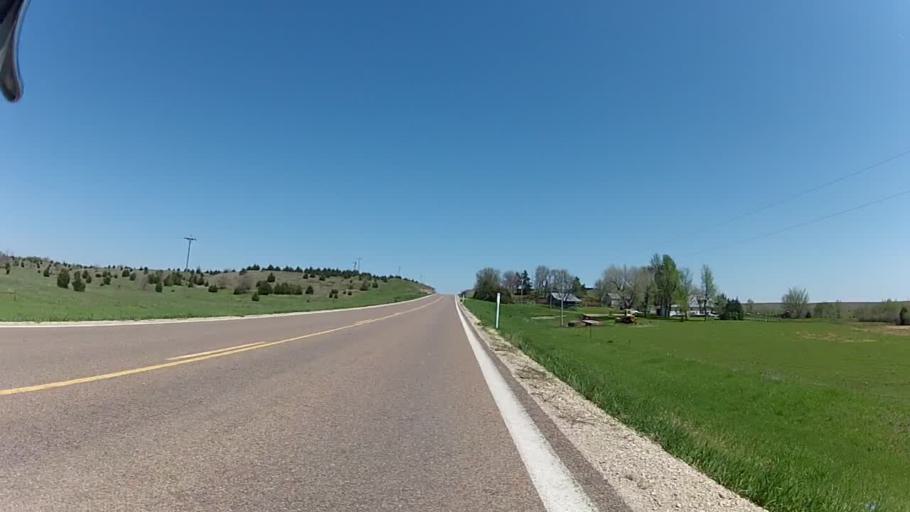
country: US
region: Kansas
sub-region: Wabaunsee County
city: Alma
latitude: 38.9230
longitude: -96.5194
